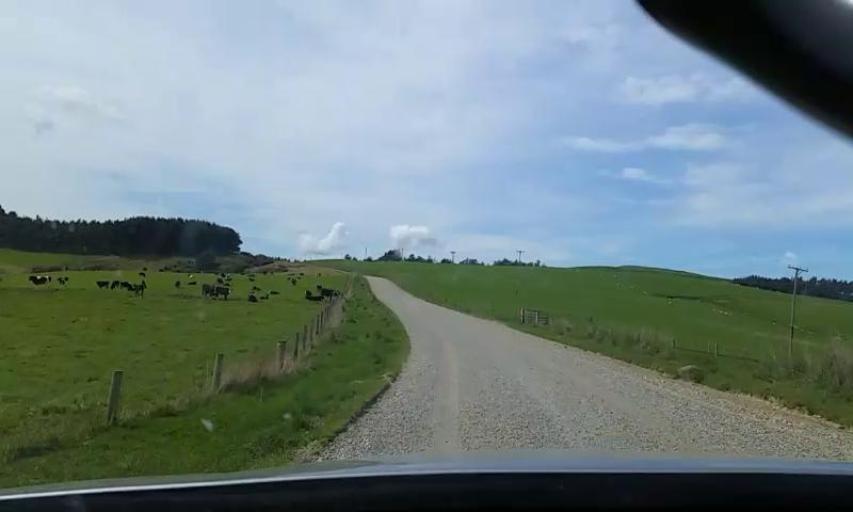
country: NZ
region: Otago
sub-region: Clutha District
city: Papatowai
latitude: -46.6351
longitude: 168.9685
